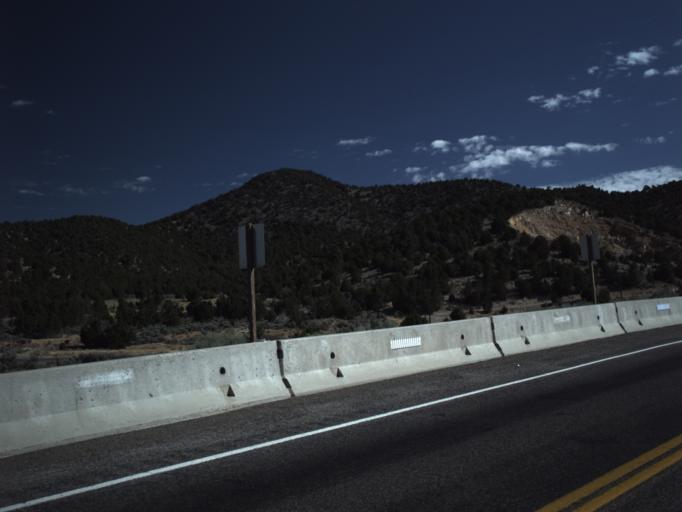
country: US
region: Utah
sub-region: Utah County
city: Genola
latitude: 39.9428
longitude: -112.1448
